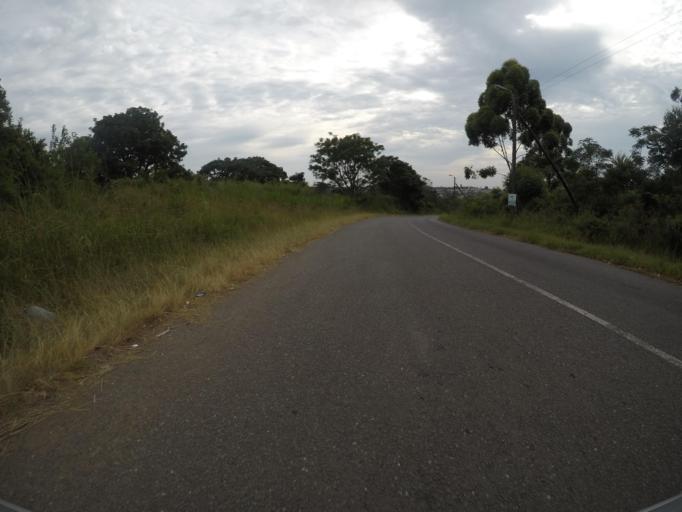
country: ZA
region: Eastern Cape
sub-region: Buffalo City Metropolitan Municipality
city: East London
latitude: -32.9724
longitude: 27.8545
